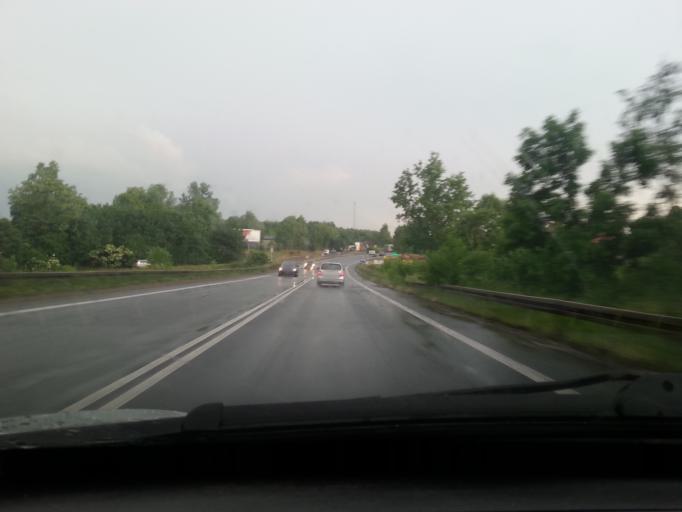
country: PL
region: Lodz Voivodeship
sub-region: Powiat zgierski
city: Strykow
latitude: 51.8443
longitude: 19.5592
